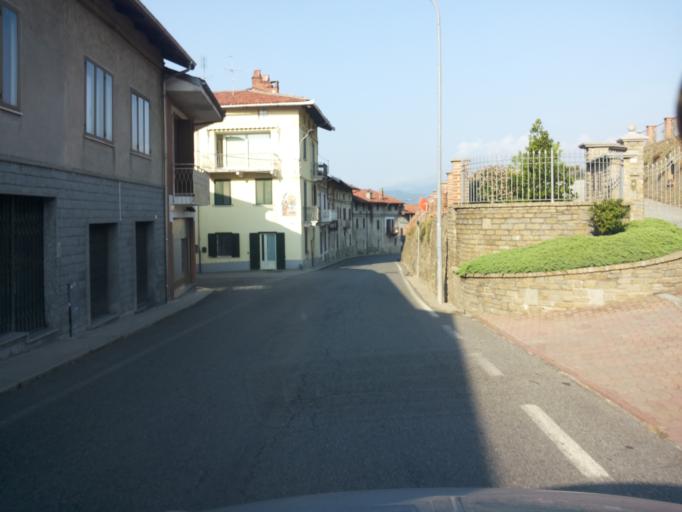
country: IT
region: Piedmont
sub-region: Provincia di Torino
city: Bollengo
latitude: 45.4708
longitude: 7.9434
